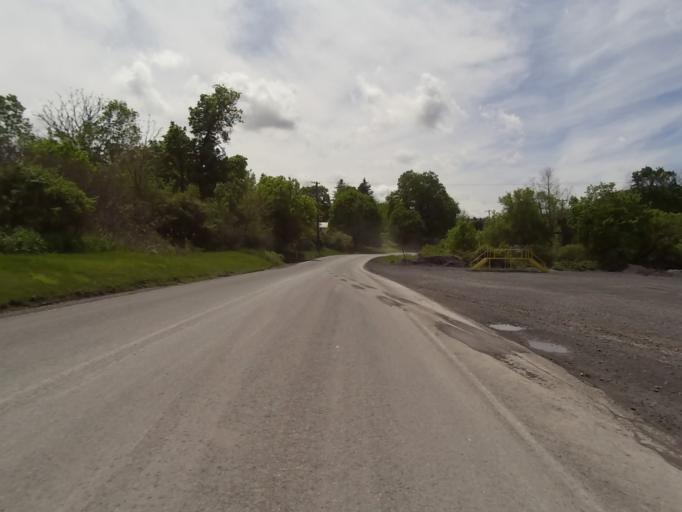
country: US
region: Pennsylvania
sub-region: Centre County
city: Lemont
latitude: 40.7977
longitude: -77.8049
